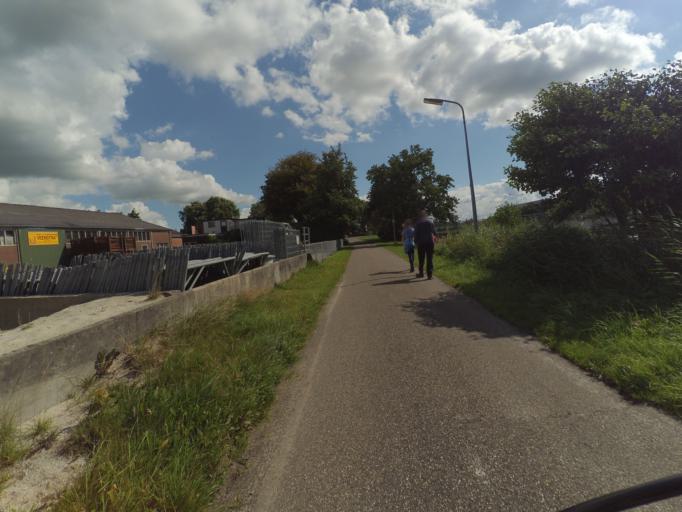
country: NL
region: Friesland
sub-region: Gemeente Achtkarspelen
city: Kootstertille
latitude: 53.2010
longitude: 6.0679
